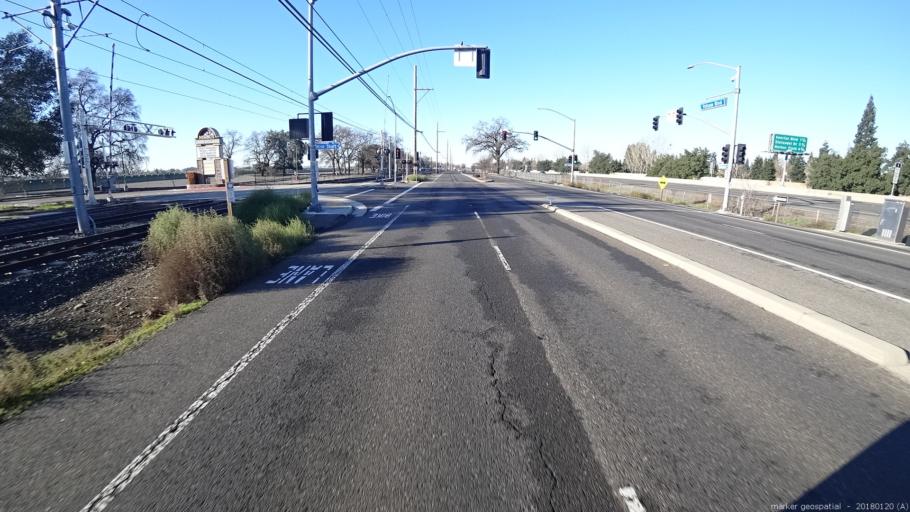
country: US
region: California
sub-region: Sacramento County
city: Gold River
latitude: 38.6208
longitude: -121.2380
